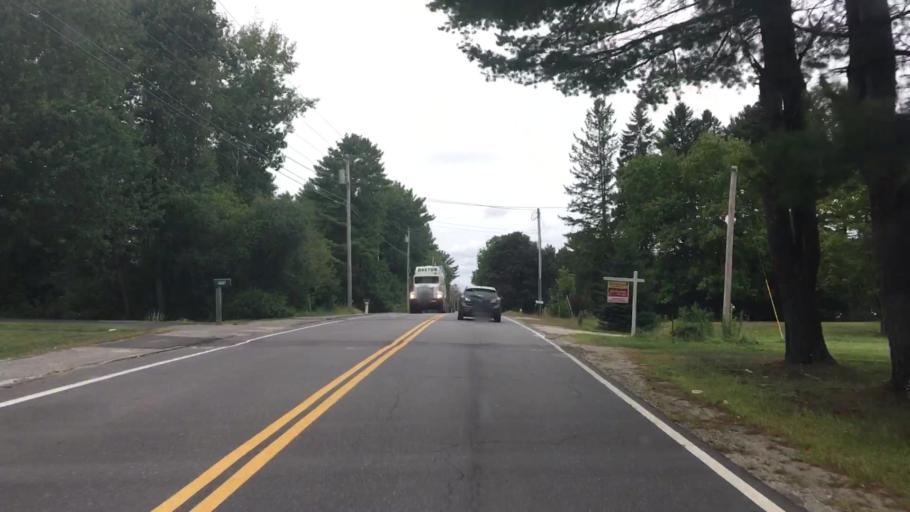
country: US
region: Maine
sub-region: Cumberland County
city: Yarmouth
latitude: 43.8143
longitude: -70.1813
